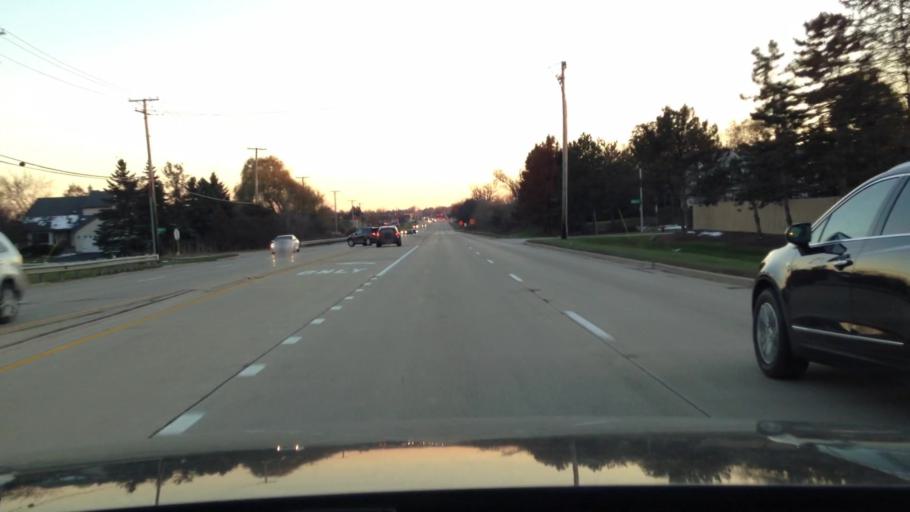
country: US
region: Illinois
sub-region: Cook County
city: Bartlett
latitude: 41.9832
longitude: -88.2073
